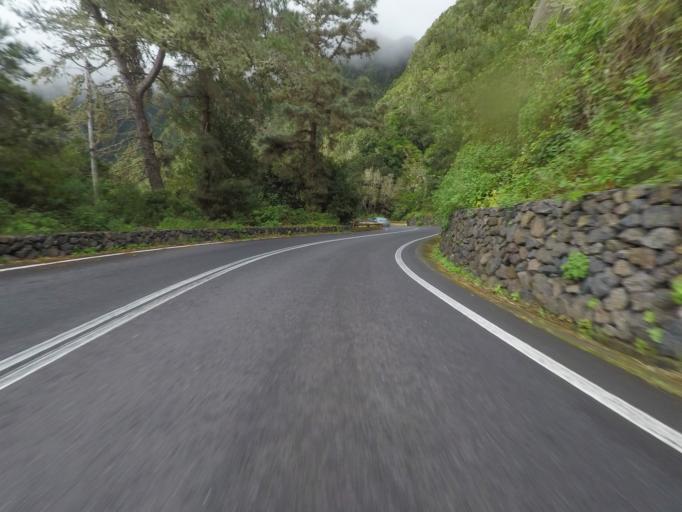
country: ES
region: Canary Islands
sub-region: Provincia de Santa Cruz de Tenerife
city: Hermigua
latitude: 28.1343
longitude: -17.1921
